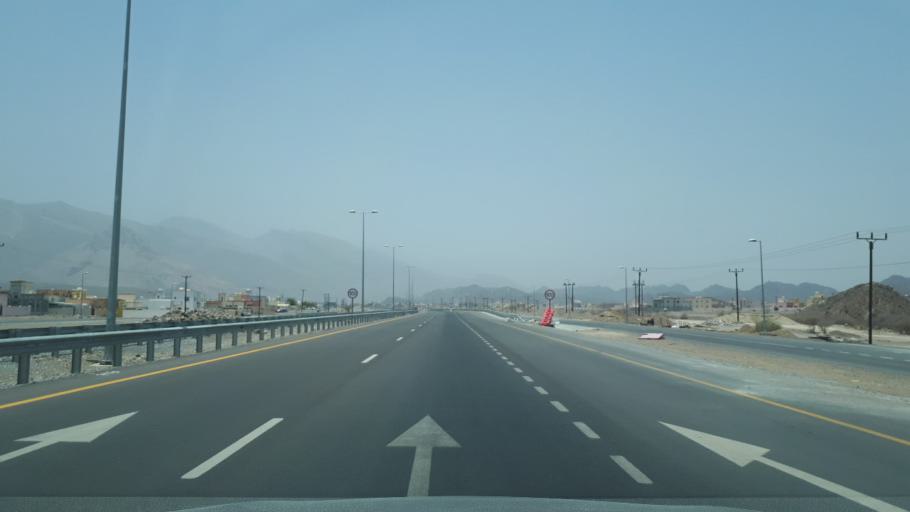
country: OM
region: Al Batinah
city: Rustaq
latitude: 23.4176
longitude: 57.3641
